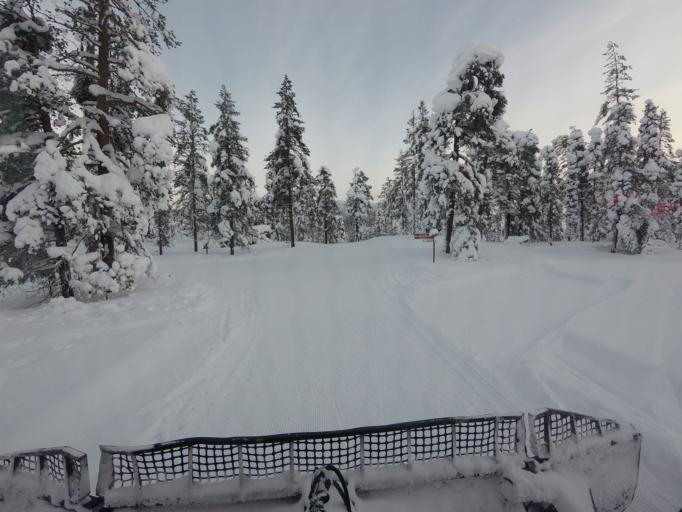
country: FI
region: Lapland
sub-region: Tunturi-Lappi
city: Kolari
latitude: 67.6556
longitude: 24.2498
